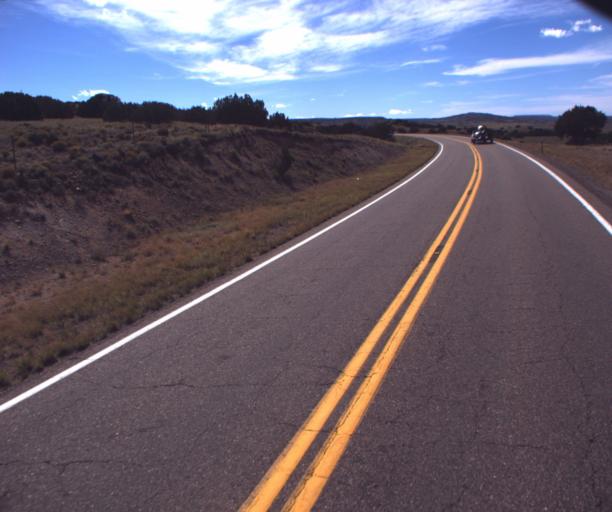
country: US
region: Arizona
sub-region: Apache County
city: Saint Johns
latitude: 34.4861
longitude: -109.5821
